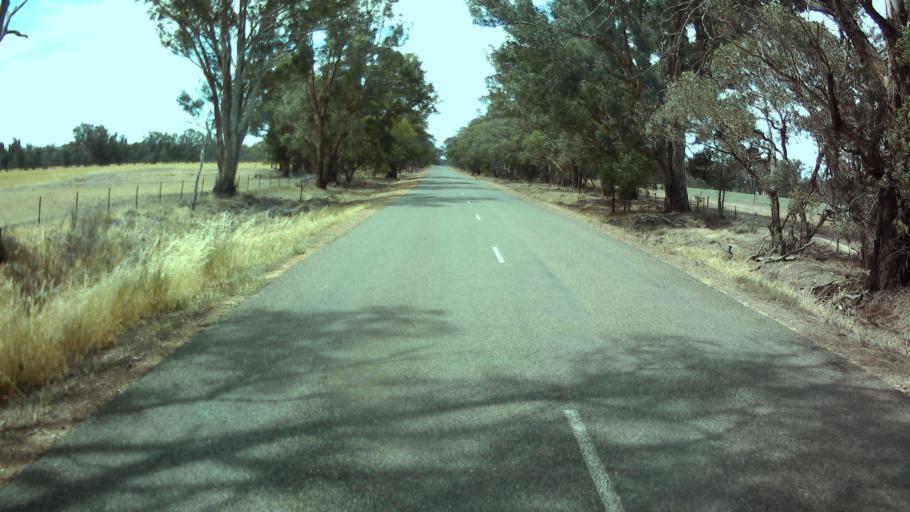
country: AU
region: New South Wales
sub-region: Weddin
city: Grenfell
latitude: -33.8022
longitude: 148.2148
